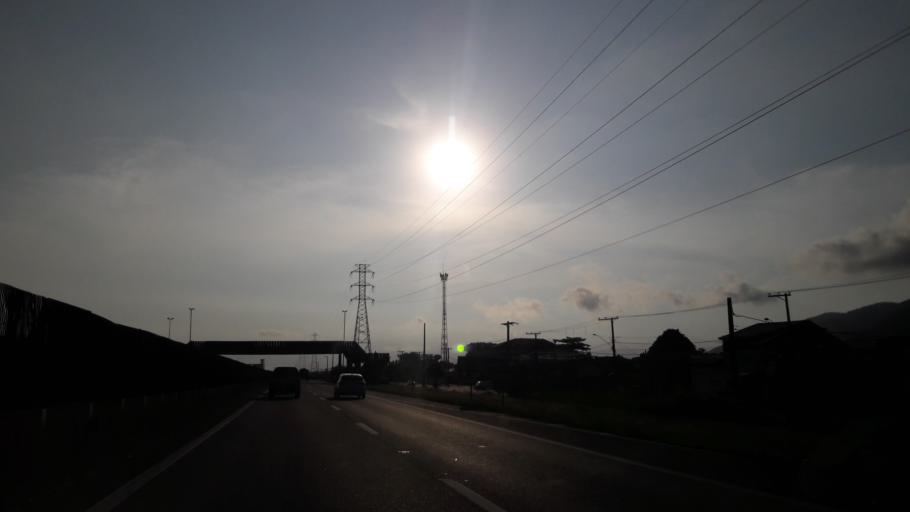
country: BR
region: Sao Paulo
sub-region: Itanhaem
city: Itanhaem
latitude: -24.1417
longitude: -46.7153
